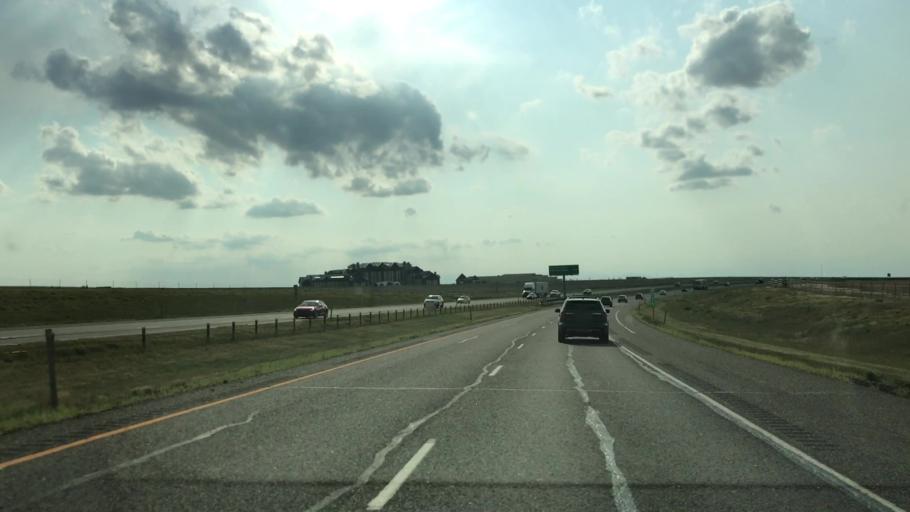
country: US
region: Colorado
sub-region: Adams County
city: Aurora
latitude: 39.8176
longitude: -104.7353
